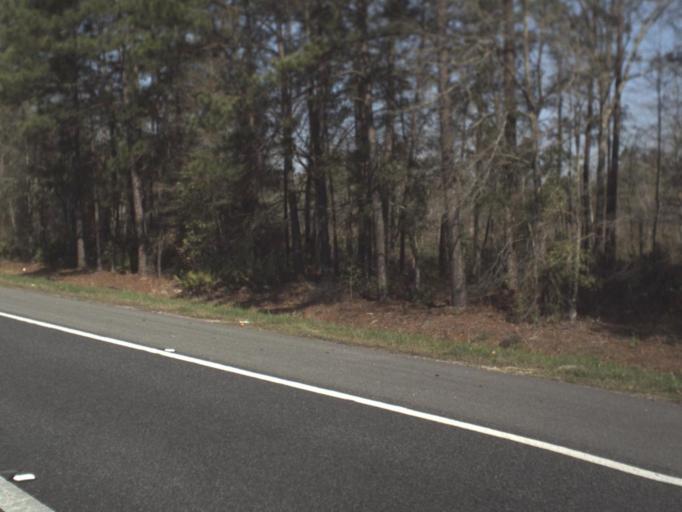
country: US
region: Florida
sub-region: Gadsden County
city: Midway
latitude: 30.4810
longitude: -84.3690
